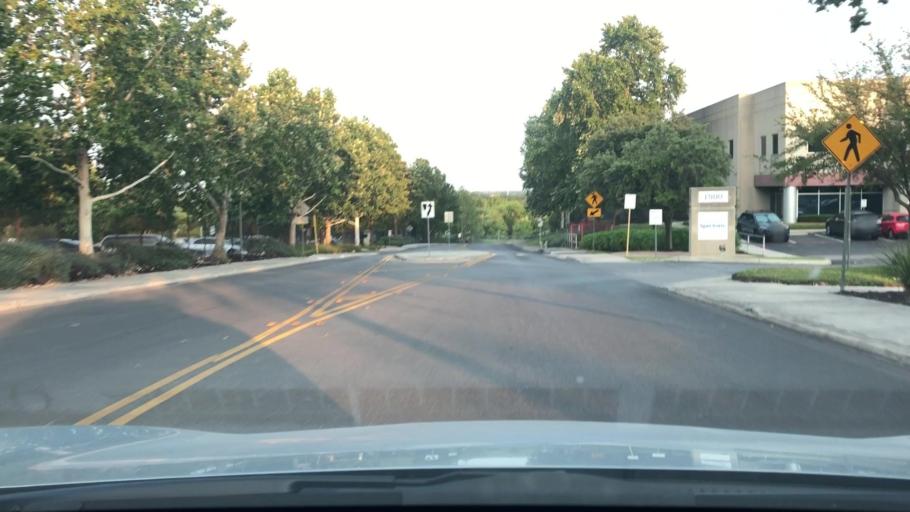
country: US
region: Texas
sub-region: Bexar County
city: Hollywood Park
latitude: 29.5539
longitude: -98.4654
